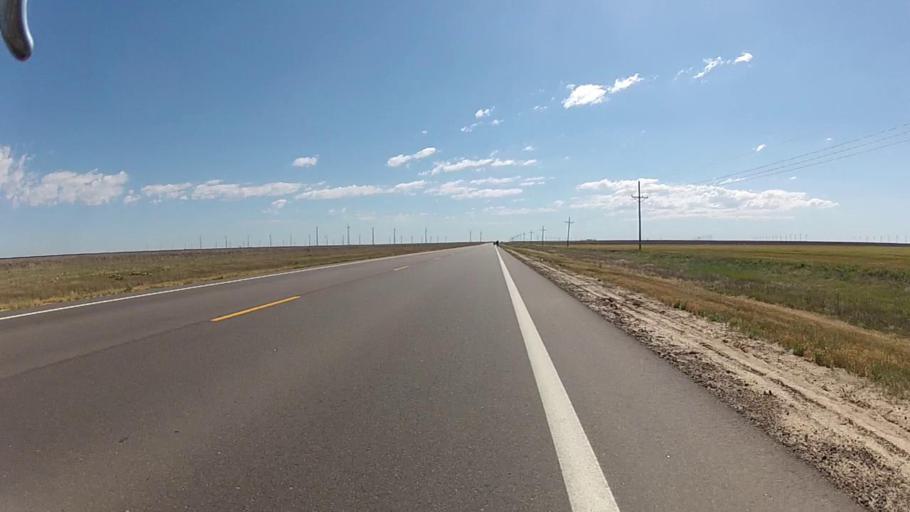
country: US
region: Kansas
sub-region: Gray County
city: Cimarron
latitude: 37.6033
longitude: -100.4279
